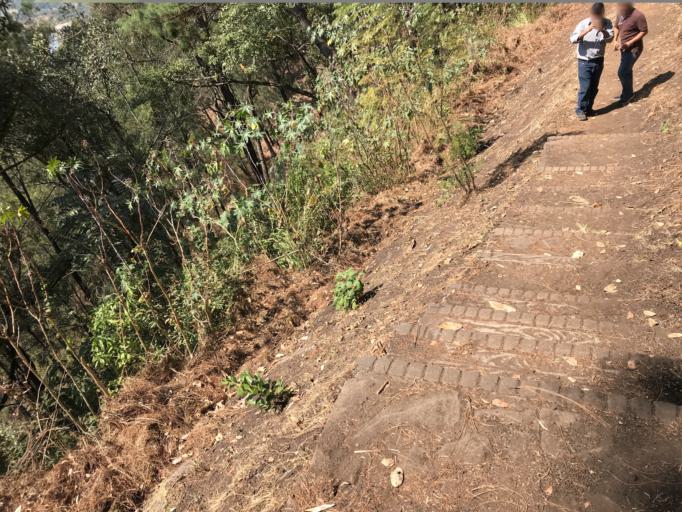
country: GT
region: Guatemala
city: Petapa
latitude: 14.4818
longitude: -90.5556
